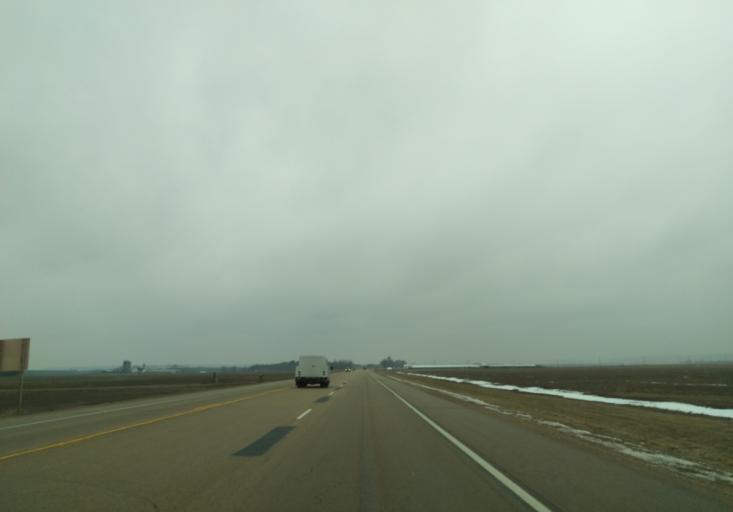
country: US
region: Wisconsin
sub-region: Sauk County
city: Spring Green
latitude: 43.1900
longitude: -90.1058
